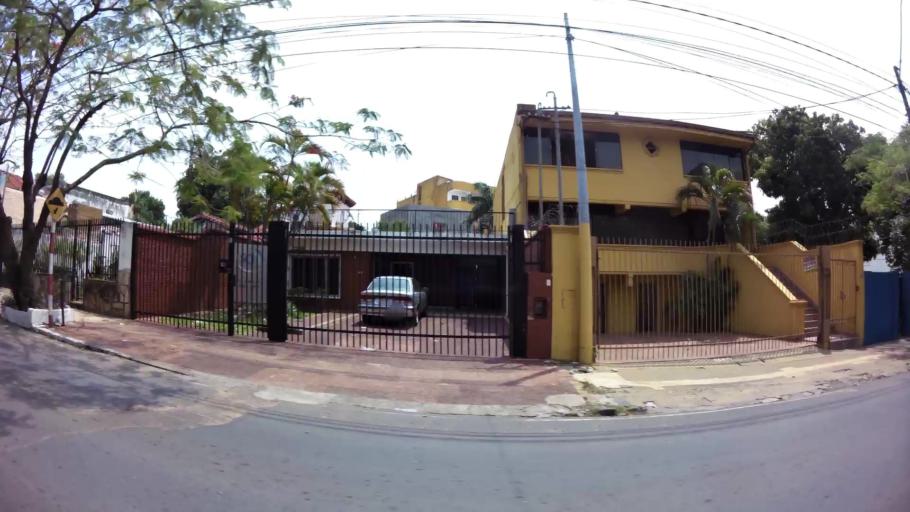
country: PY
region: Asuncion
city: Asuncion
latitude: -25.2792
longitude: -57.6001
